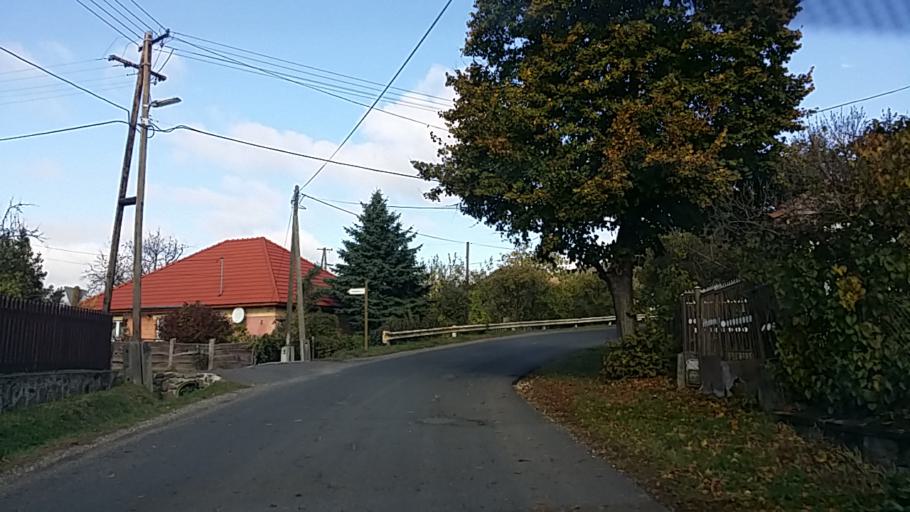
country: HU
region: Borsod-Abauj-Zemplen
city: Gonc
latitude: 48.3924
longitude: 21.2870
